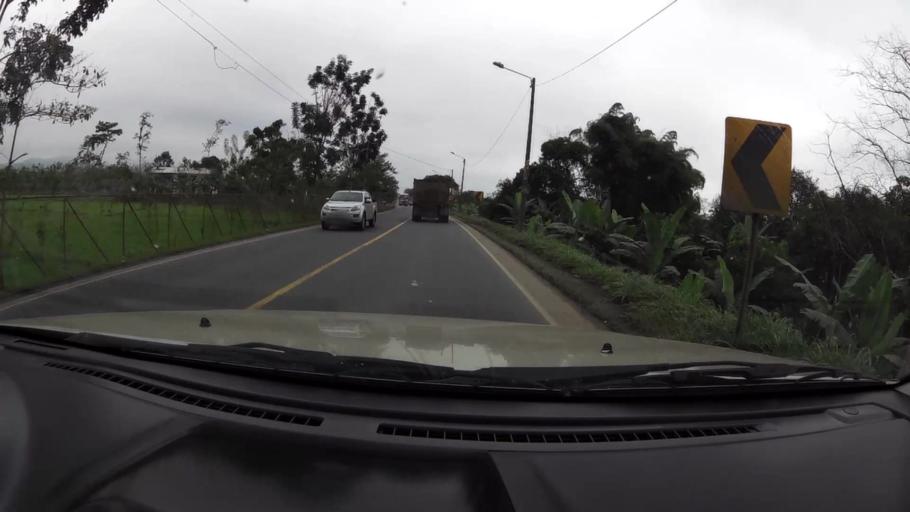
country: EC
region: Guayas
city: Balao
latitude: -3.0907
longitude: -79.7622
